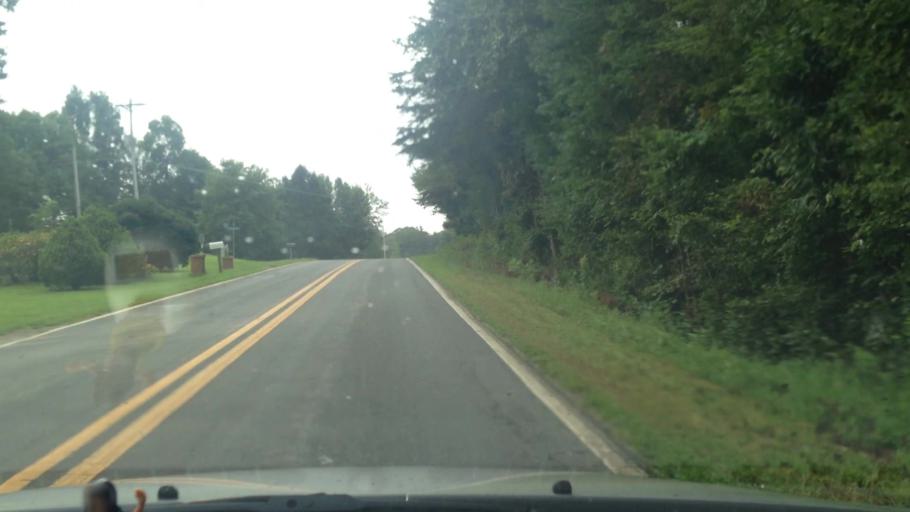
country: US
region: North Carolina
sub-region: Stokes County
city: Danbury
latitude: 36.3870
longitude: -80.1353
